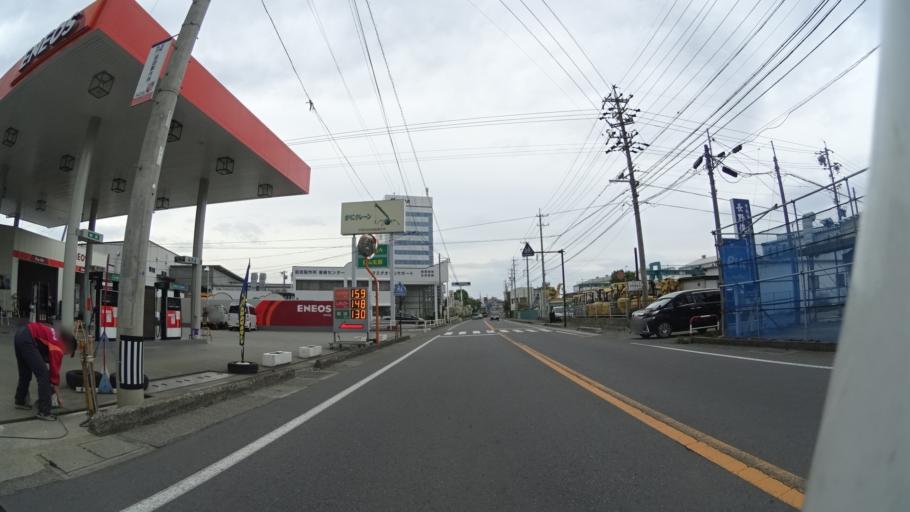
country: JP
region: Nagano
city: Nagano-shi
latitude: 36.5704
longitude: 138.1418
